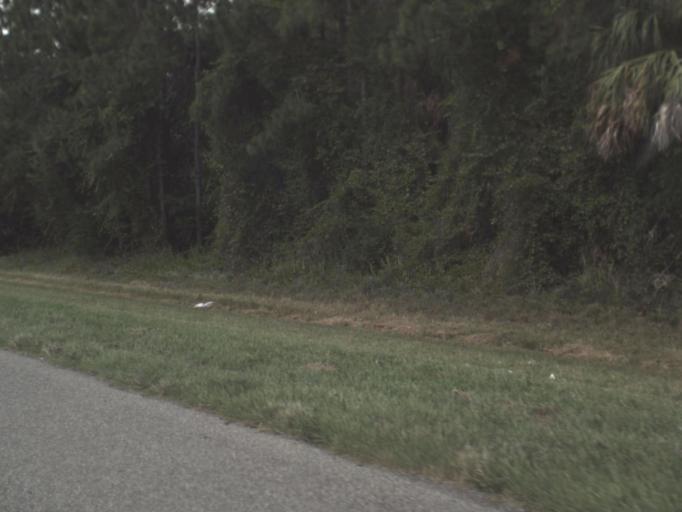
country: US
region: Florida
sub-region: Hillsborough County
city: Apollo Beach
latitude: 27.7754
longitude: -82.3622
